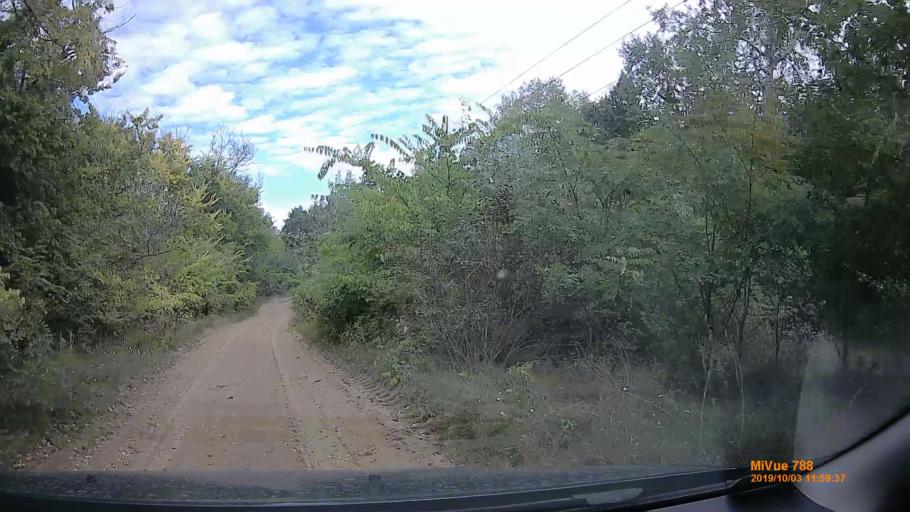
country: HU
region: Pest
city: God
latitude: 47.6713
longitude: 19.1720
